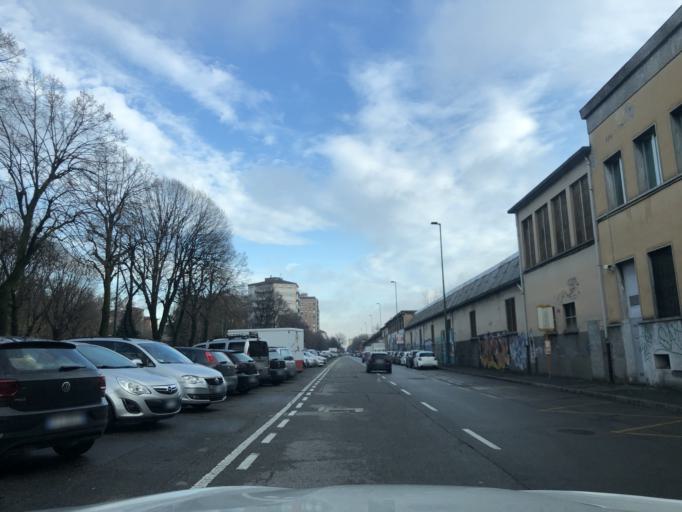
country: IT
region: Lombardy
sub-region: Citta metropolitana di Milano
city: Sesto San Giovanni
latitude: 45.5293
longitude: 9.2378
